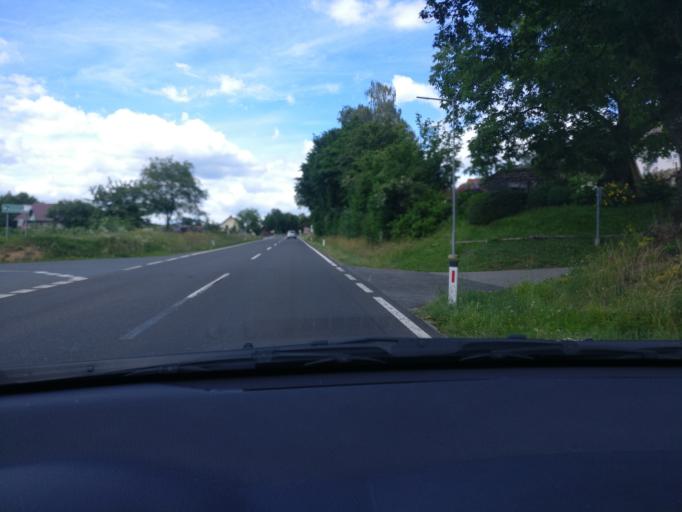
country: AT
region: Styria
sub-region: Politischer Bezirk Hartberg-Fuerstenfeld
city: Kaibing
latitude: 47.2012
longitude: 15.8415
